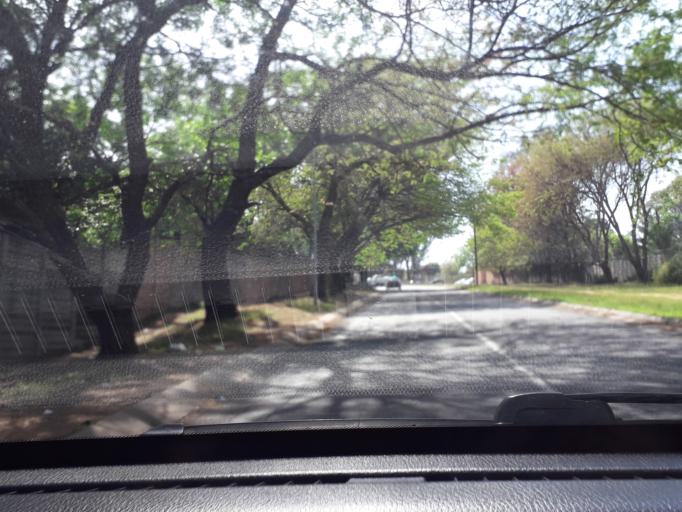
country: ZA
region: Gauteng
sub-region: City of Johannesburg Metropolitan Municipality
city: Midrand
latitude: -26.0481
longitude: 28.0696
